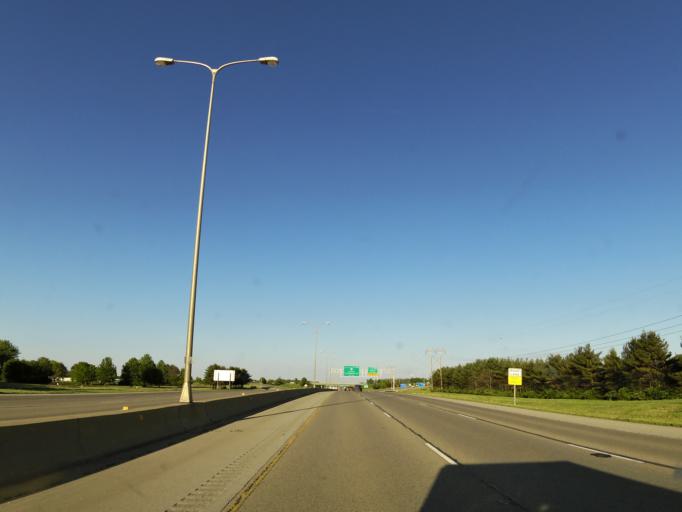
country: US
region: Illinois
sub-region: Champaign County
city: Champaign
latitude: 40.1349
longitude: -88.2259
